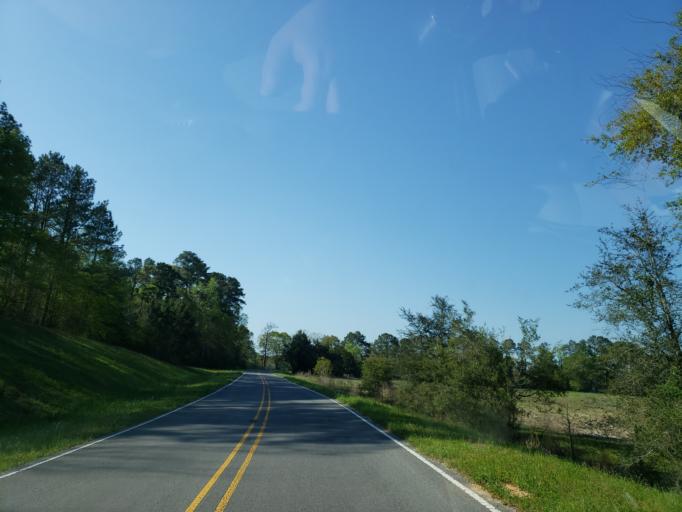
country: US
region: Mississippi
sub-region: Smith County
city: Taylorsville
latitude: 31.6872
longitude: -89.4123
